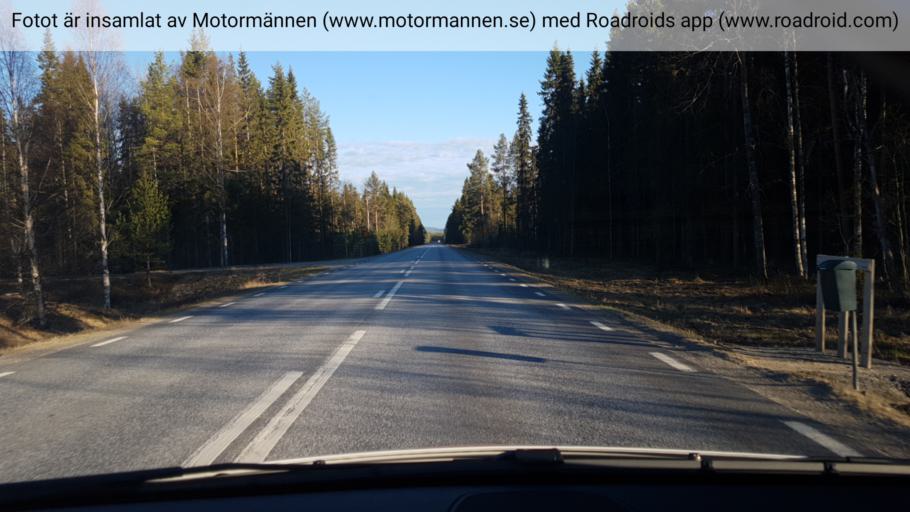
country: SE
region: Vaesterbotten
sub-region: Vannas Kommun
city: Vaennaes
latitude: 63.9606
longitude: 19.7523
